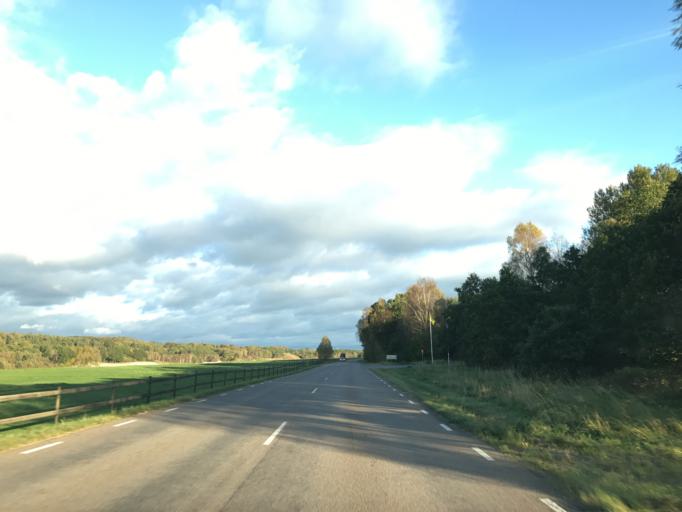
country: SE
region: Skane
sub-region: Klippans Kommun
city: Ljungbyhed
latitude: 56.1426
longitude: 13.2632
